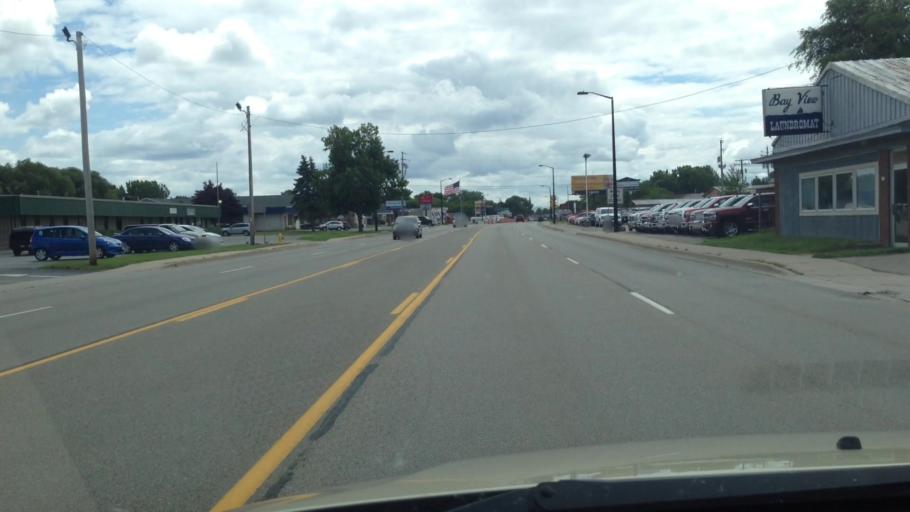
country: US
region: Michigan
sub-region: Menominee County
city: Menominee
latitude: 45.1237
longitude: -87.6132
